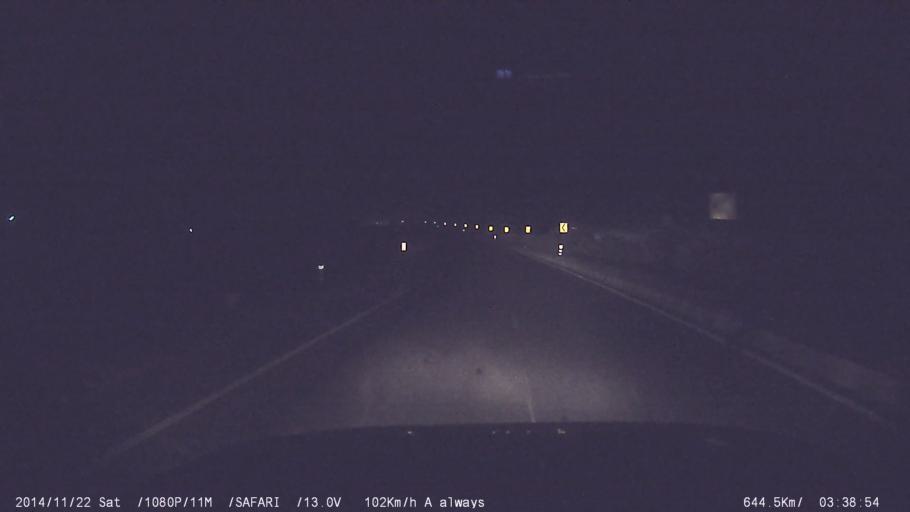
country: IN
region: Tamil Nadu
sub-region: Namakkal
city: Tiruchengode
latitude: 11.4704
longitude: 77.8262
